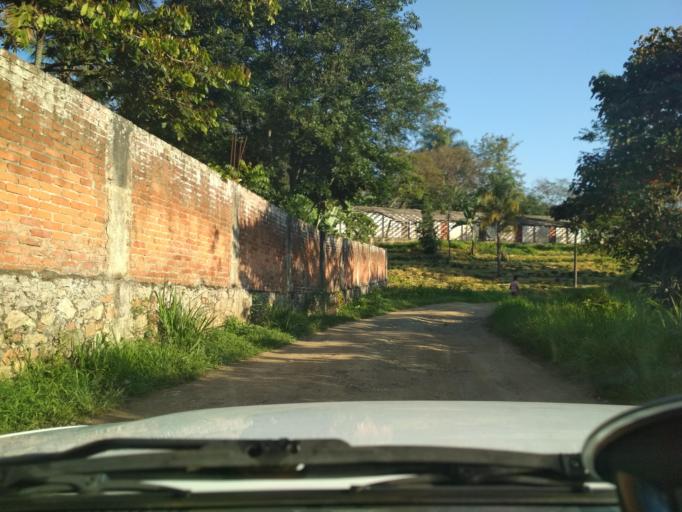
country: MX
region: Veracruz
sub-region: Fortin
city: Fraccionamiento Villas de la Llave
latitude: 18.9261
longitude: -96.9918
